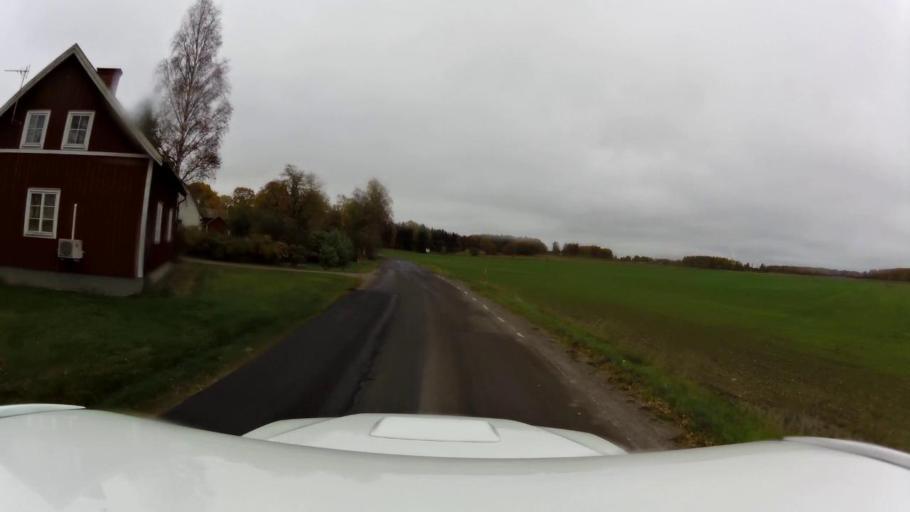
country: SE
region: OEstergoetland
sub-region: Linkopings Kommun
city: Ekangen
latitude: 58.4543
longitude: 15.7029
